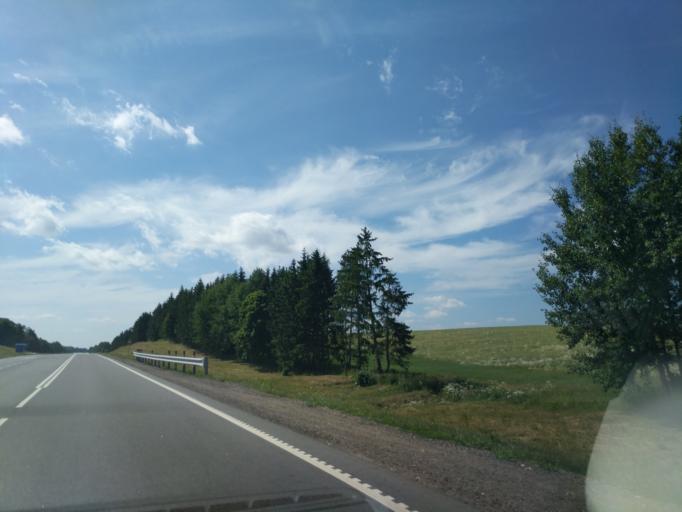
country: BY
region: Minsk
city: Syomkava
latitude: 54.1151
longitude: 27.4321
